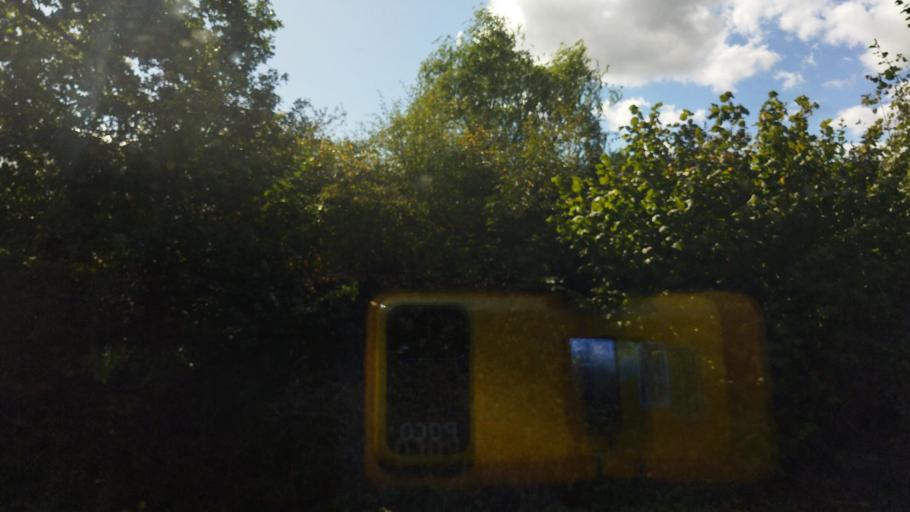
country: DE
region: North Rhine-Westphalia
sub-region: Regierungsbezirk Munster
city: Rheine
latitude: 52.2835
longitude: 7.4266
